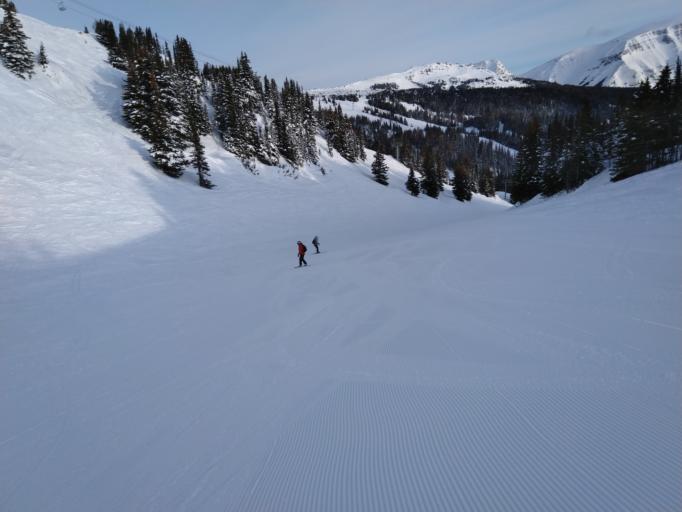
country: CA
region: Alberta
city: Banff
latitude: 51.0732
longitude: -115.7835
